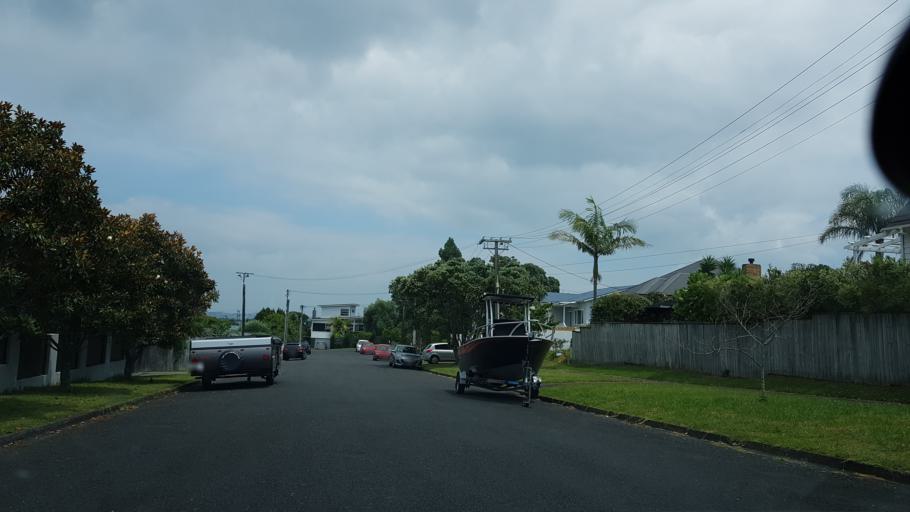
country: NZ
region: Auckland
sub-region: Auckland
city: North Shore
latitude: -36.8001
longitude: 174.7787
